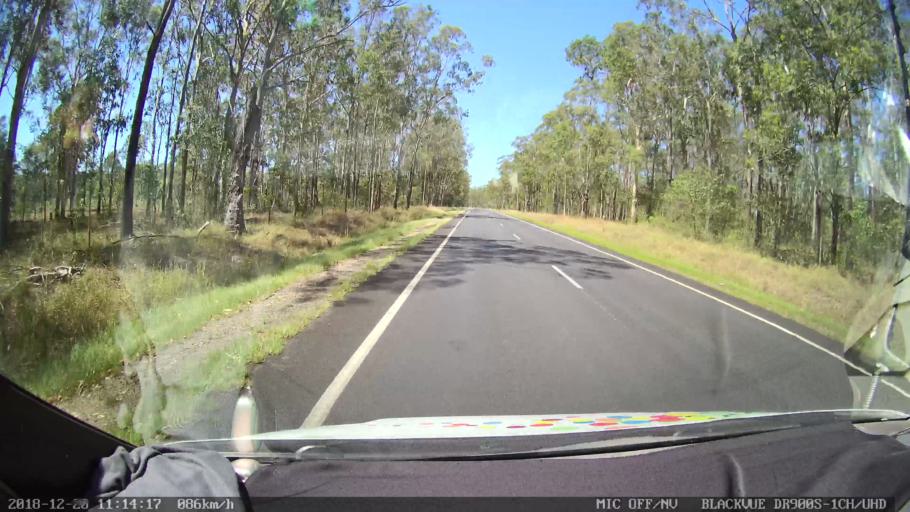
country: AU
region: New South Wales
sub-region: Richmond Valley
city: Casino
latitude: -28.9987
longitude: 153.0095
